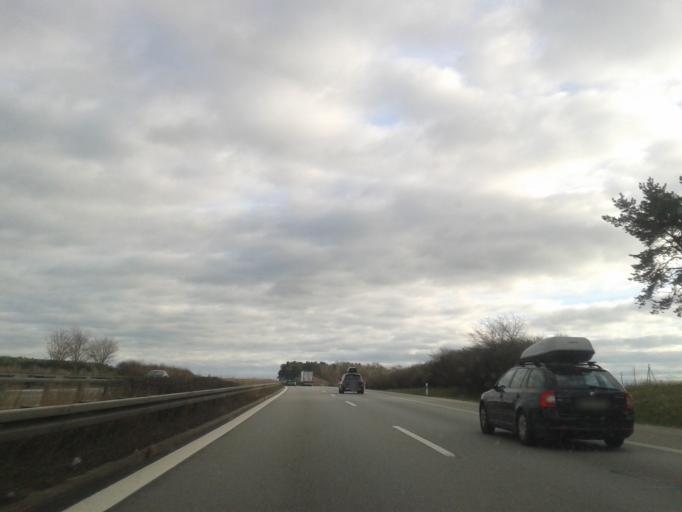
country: DE
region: Saxony
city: Guttau
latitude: 51.2091
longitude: 14.5836
